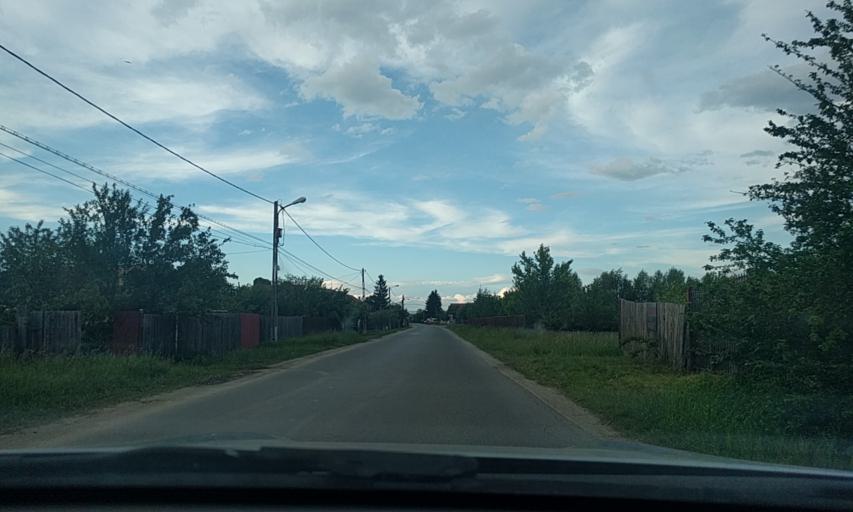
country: RO
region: Brasov
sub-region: Comuna Harman
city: Harman
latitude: 45.7589
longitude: 25.7205
